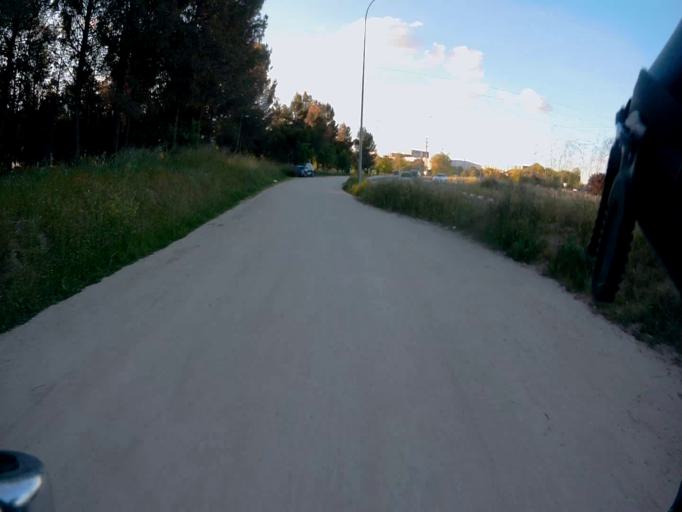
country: ES
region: Madrid
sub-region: Provincia de Madrid
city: Leganes
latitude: 40.3231
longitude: -3.7884
